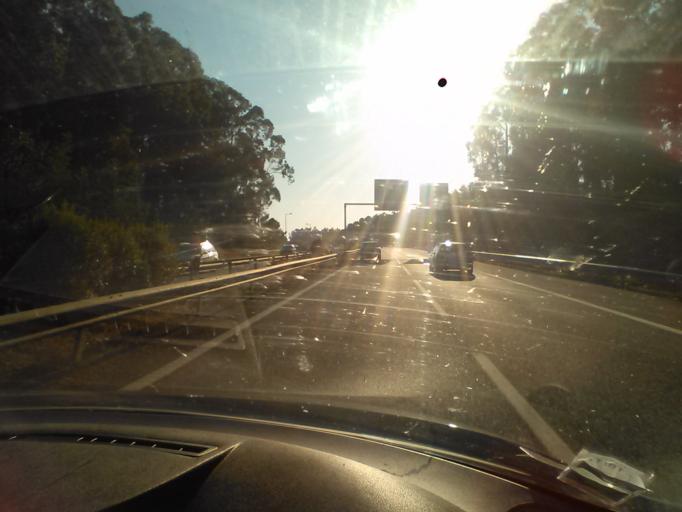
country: PT
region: Porto
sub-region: Santo Tirso
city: Aves
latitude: 41.4021
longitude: -8.4570
